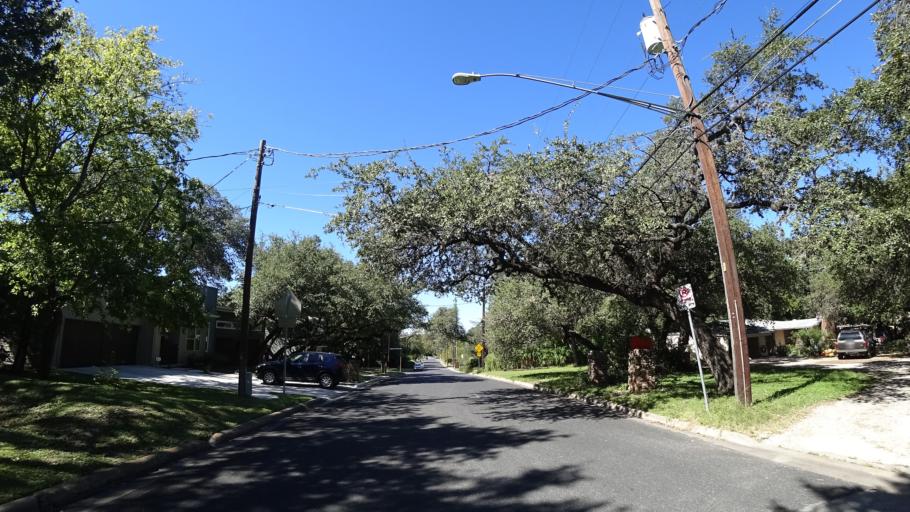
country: US
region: Texas
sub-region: Travis County
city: Austin
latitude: 30.2309
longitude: -97.7707
